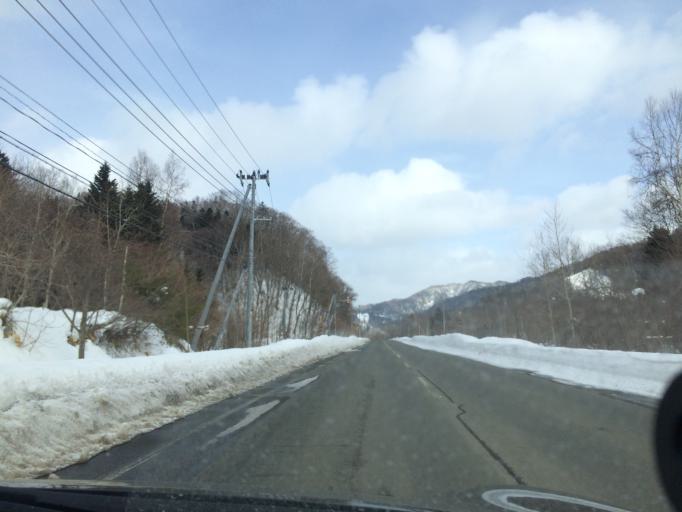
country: JP
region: Hokkaido
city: Shimo-furano
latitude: 43.0152
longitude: 142.4248
